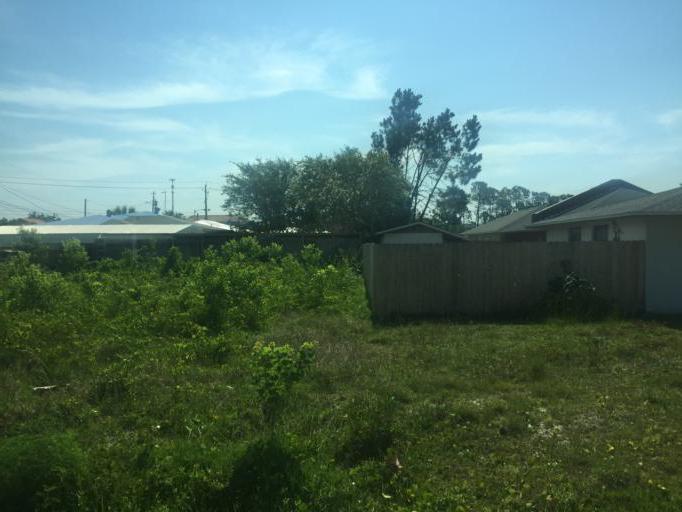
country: US
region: Florida
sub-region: Bay County
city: Lower Grand Lagoon
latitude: 30.1577
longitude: -85.7542
